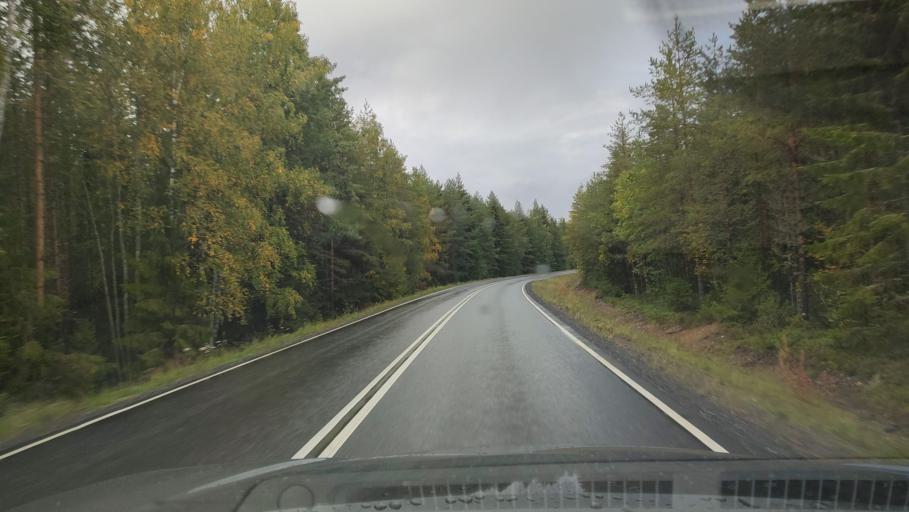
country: FI
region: Southern Ostrobothnia
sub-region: Suupohja
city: Karijoki
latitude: 62.2875
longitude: 21.6241
